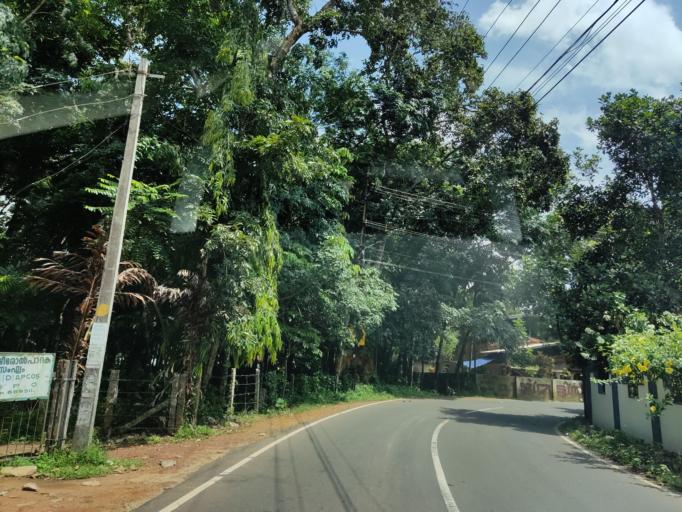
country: IN
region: Kerala
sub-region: Alappuzha
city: Mavelikara
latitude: 9.2841
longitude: 76.5702
